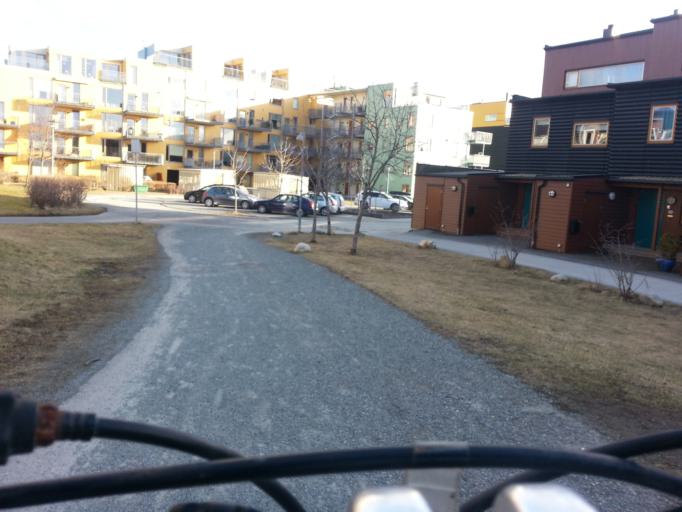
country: NO
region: Sor-Trondelag
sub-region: Trondheim
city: Trondheim
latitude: 63.4493
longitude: 10.4442
